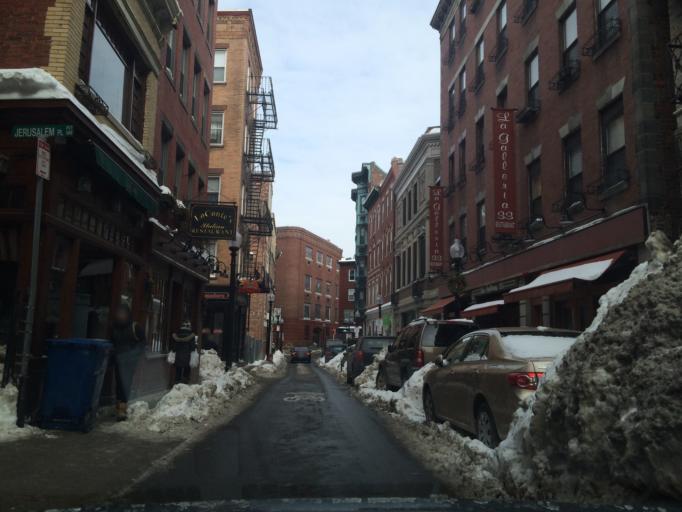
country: US
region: Massachusetts
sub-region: Suffolk County
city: Boston
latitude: 42.3644
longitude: -71.0556
